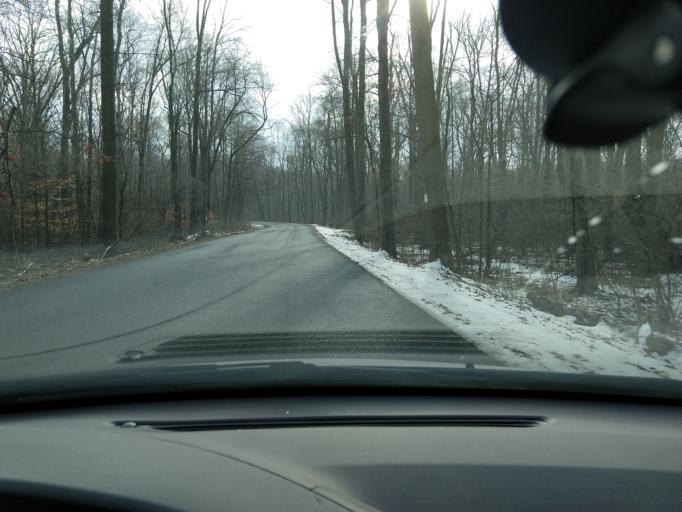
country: US
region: Pennsylvania
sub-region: Chester County
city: Elverson
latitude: 40.1945
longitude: -75.7945
